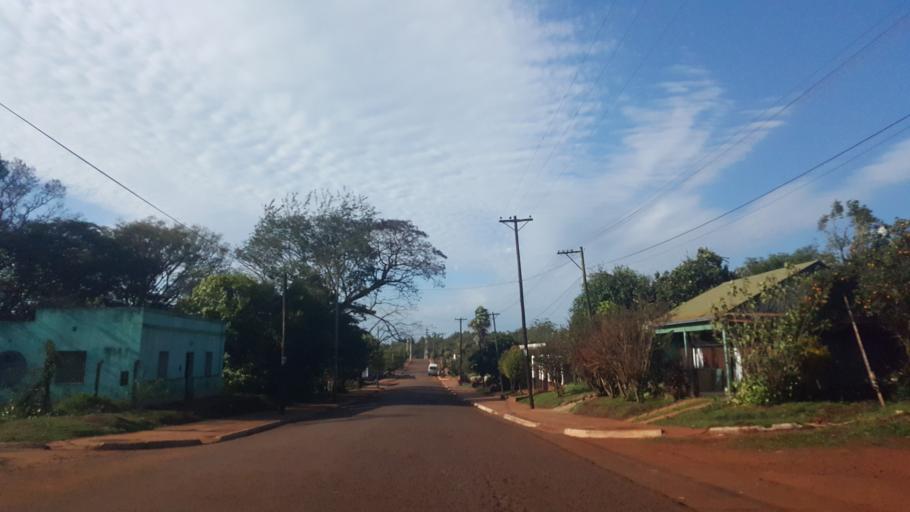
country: AR
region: Misiones
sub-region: Departamento de San Ignacio
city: San Ignacio
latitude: -27.2536
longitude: -55.5289
